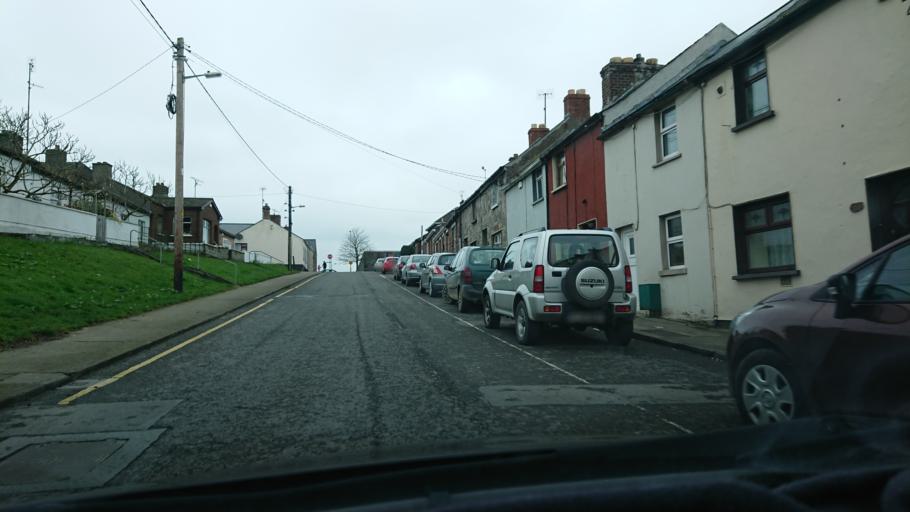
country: IE
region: Leinster
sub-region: Lu
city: Drogheda
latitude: 53.7177
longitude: -6.3474
